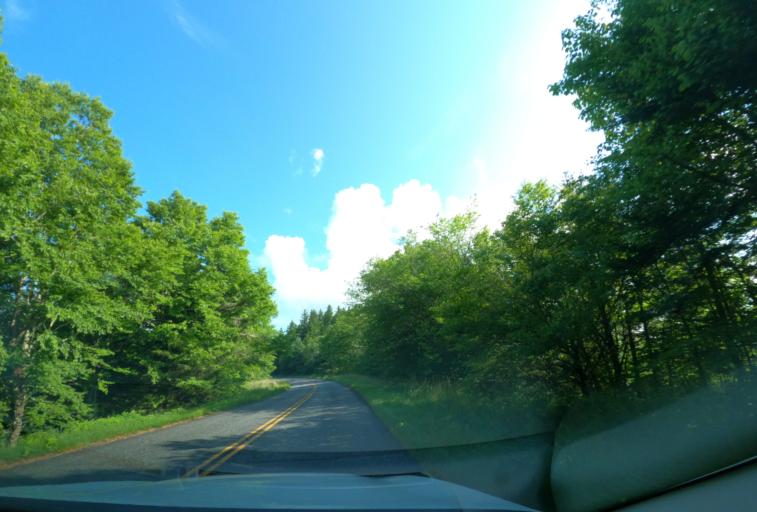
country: US
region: North Carolina
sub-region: Haywood County
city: Hazelwood
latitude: 35.3305
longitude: -82.9652
